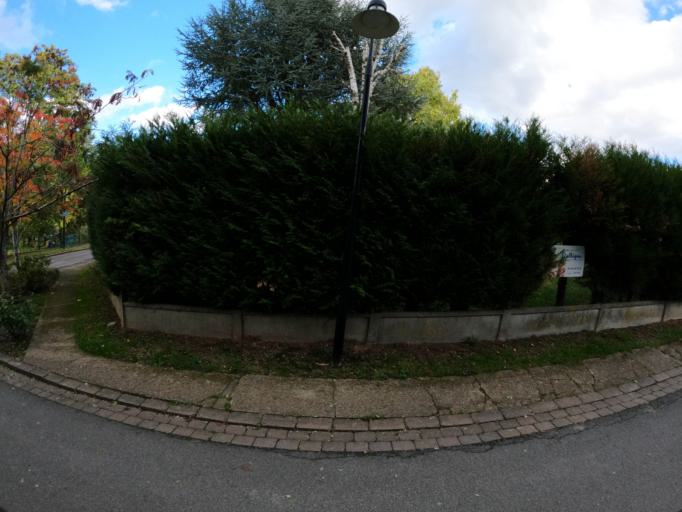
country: FR
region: Ile-de-France
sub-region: Departement de Seine-et-Marne
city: Chessy
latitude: 48.8826
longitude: 2.7658
